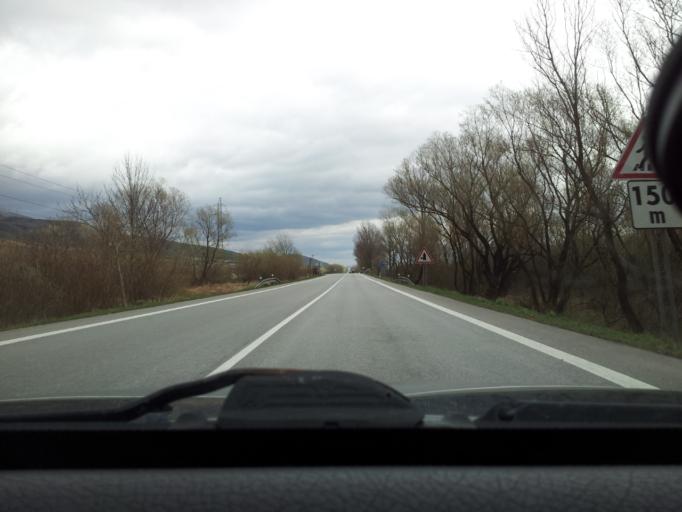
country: SK
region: Kosicky
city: Medzev
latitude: 48.6012
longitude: 20.7452
